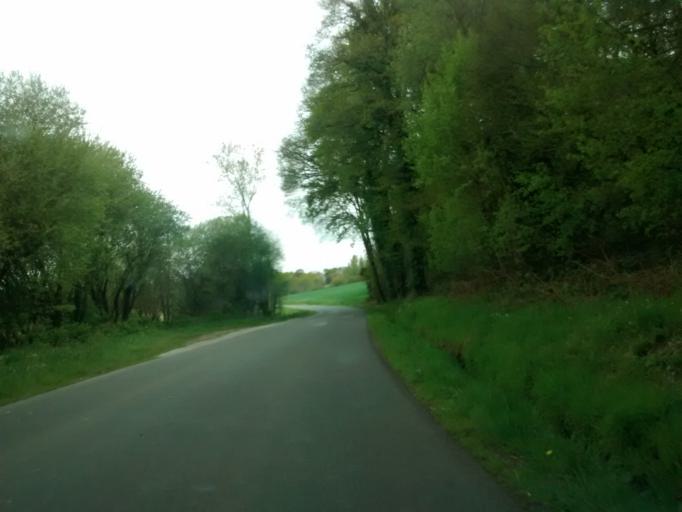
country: FR
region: Brittany
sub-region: Departement du Morbihan
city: Ruffiac
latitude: 47.7844
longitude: -2.3148
